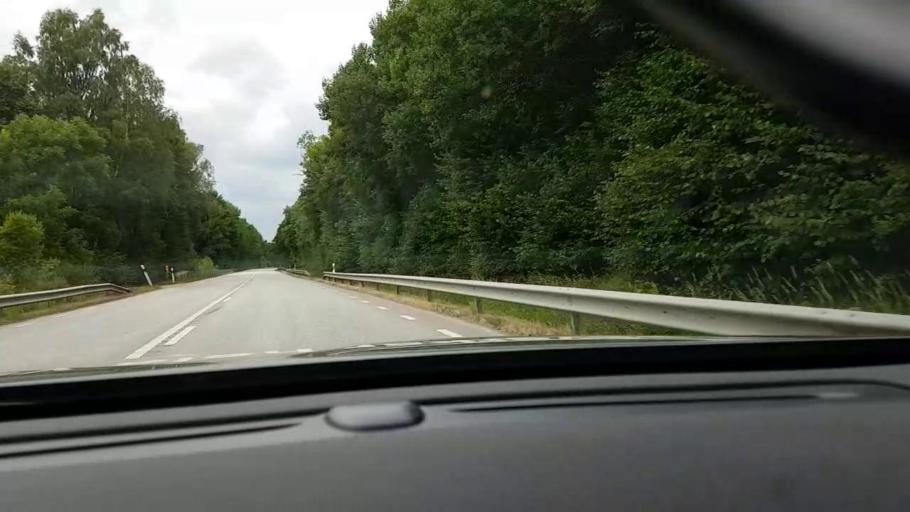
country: SE
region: Skane
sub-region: Horby Kommun
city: Hoerby
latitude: 55.8696
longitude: 13.6366
